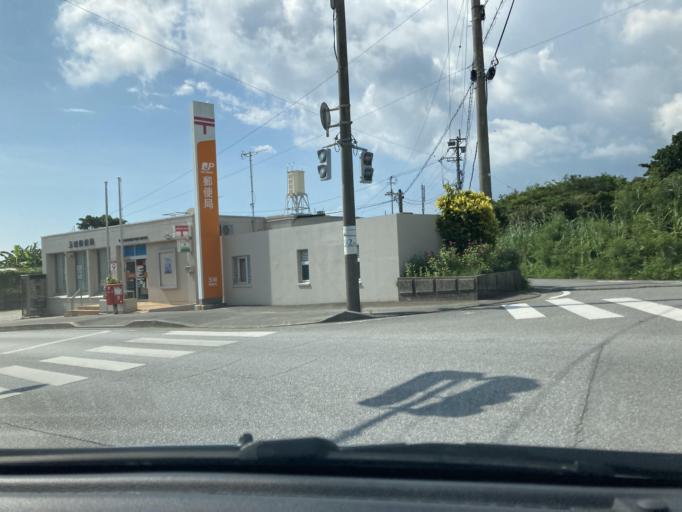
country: JP
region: Okinawa
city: Tomigusuku
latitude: 26.1452
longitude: 127.7641
